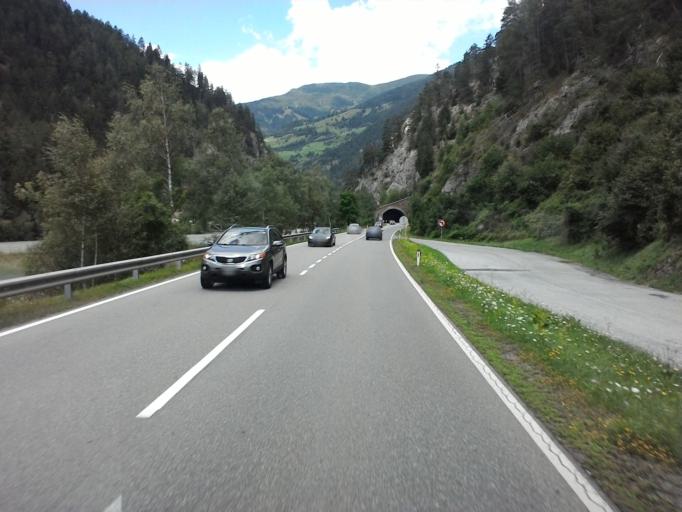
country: AT
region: Tyrol
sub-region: Politischer Bezirk Landeck
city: Prutz
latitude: 47.1034
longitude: 10.6635
